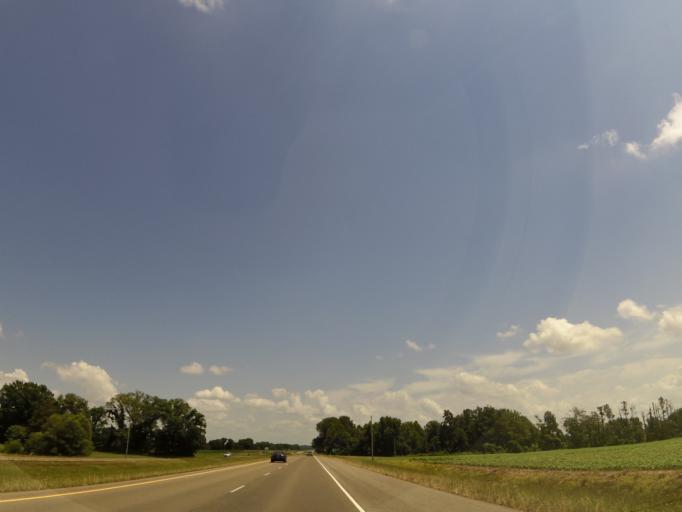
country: US
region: Tennessee
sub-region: Crockett County
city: Alamo
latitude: 35.8699
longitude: -89.2150
